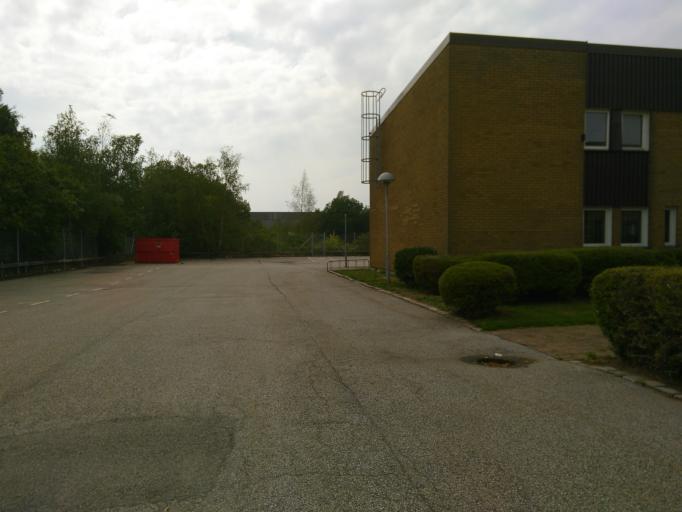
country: SE
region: Skane
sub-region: Landskrona
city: Landskrona
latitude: 55.8676
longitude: 12.8382
